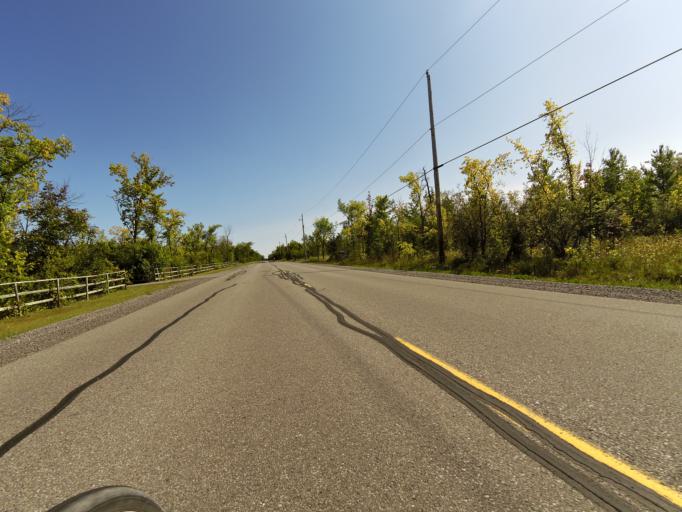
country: CA
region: Ontario
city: Bells Corners
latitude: 45.4298
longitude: -75.9587
